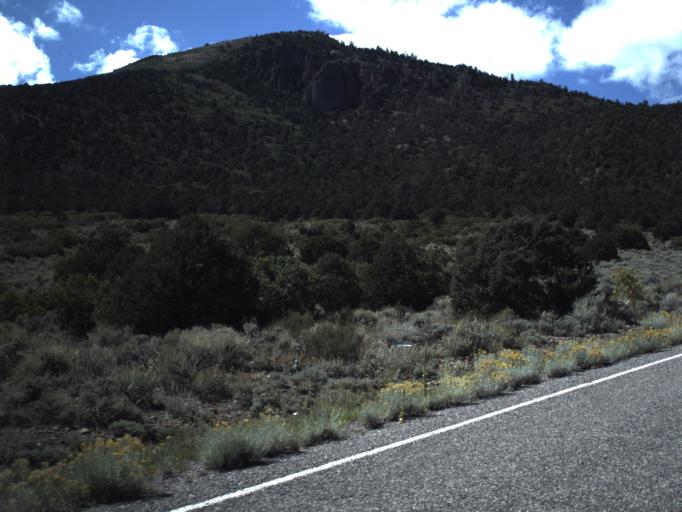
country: US
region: Utah
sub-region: Piute County
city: Junction
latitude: 38.2641
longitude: -112.3011
